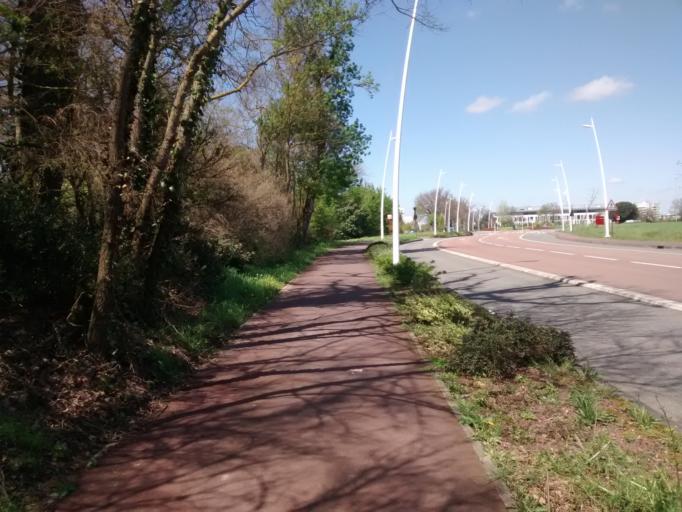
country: FR
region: Midi-Pyrenees
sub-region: Departement de la Haute-Garonne
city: Labege
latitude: 43.5337
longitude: 1.5218
